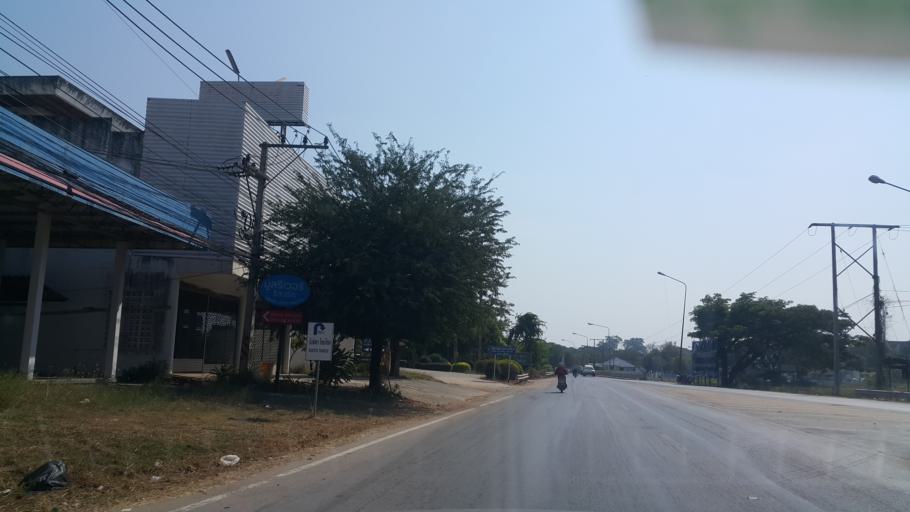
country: TH
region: Nakhon Ratchasima
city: Phimai
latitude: 15.2272
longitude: 102.4944
